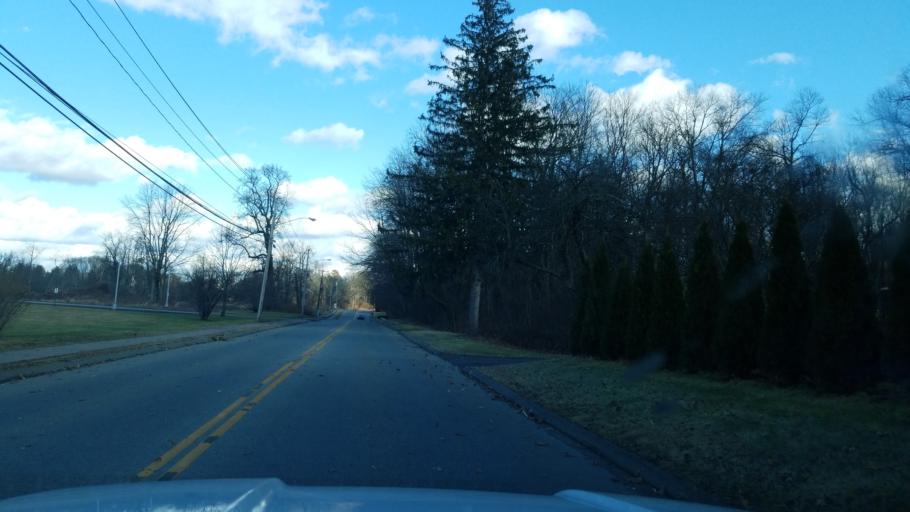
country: US
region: Connecticut
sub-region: Middlesex County
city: Middletown
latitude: 41.5434
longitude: -72.6650
